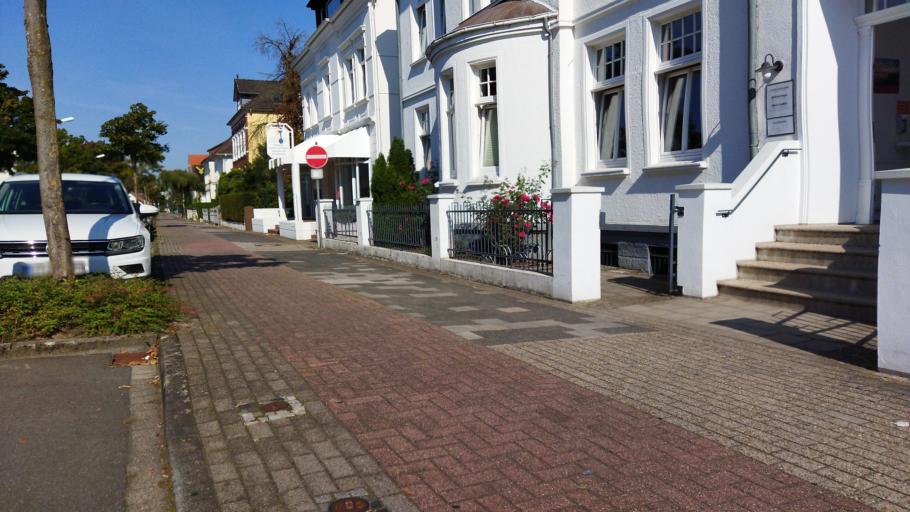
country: DE
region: North Rhine-Westphalia
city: Lengerich
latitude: 52.1848
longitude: 7.8623
